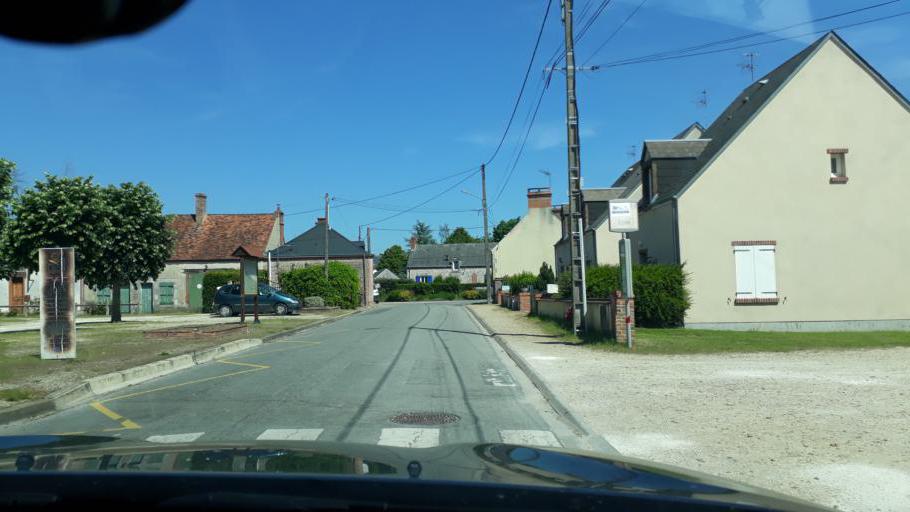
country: FR
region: Centre
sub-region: Departement du Loiret
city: Saint-Benoit-sur-Loire
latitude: 47.8040
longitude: 2.2760
